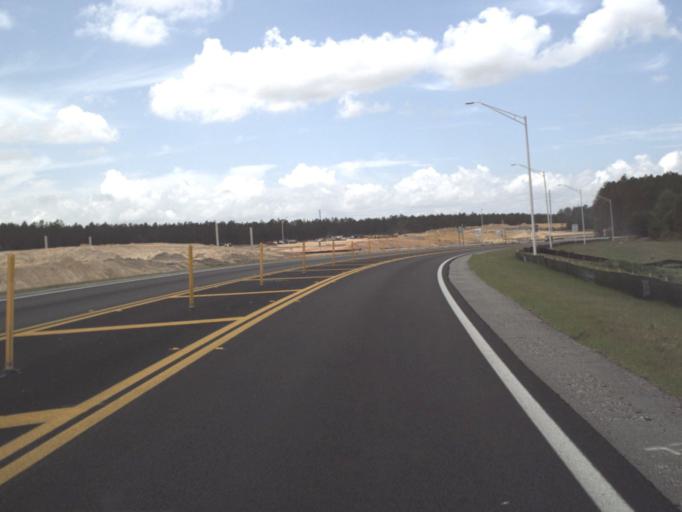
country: US
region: Florida
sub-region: Lake County
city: Mount Plymouth
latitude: 28.7803
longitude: -81.5241
